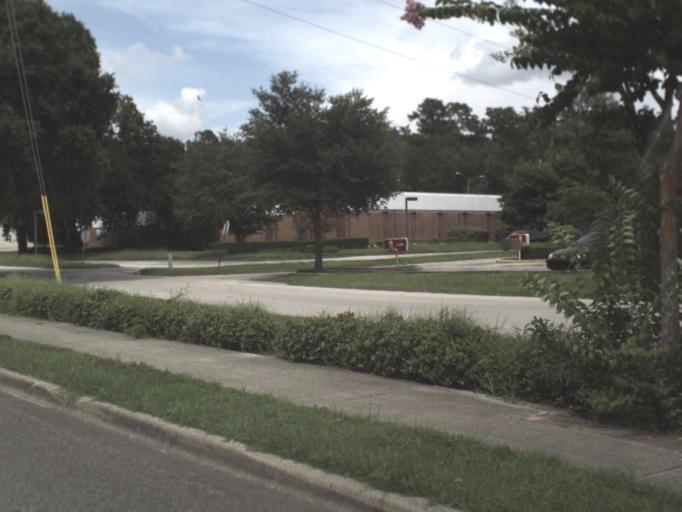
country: US
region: Florida
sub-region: Hernando County
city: South Brooksville
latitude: 28.5432
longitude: -82.4021
